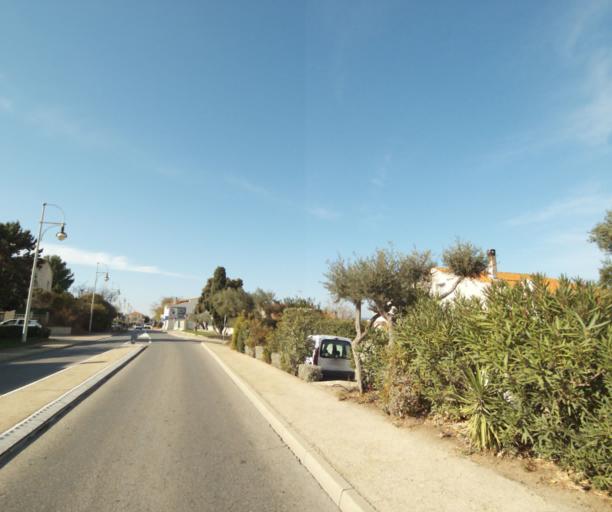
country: FR
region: Provence-Alpes-Cote d'Azur
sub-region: Departement des Bouches-du-Rhone
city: Chateauneuf-les-Martigues
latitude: 43.3971
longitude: 5.1147
